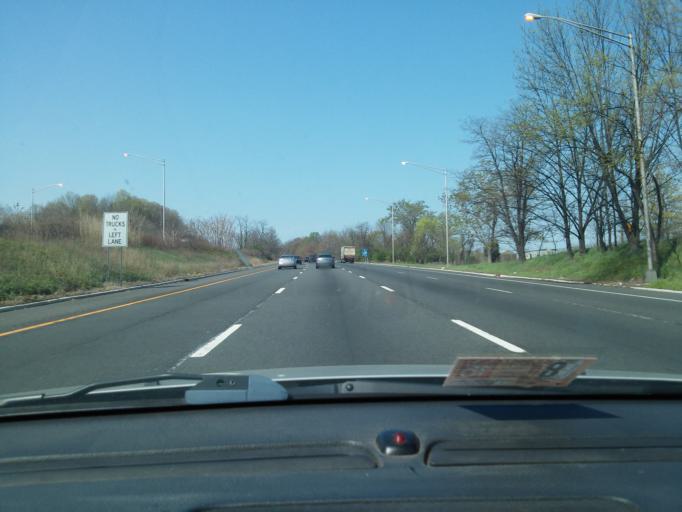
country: US
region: New Jersey
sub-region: Union County
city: Springfield
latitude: 40.7098
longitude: -74.3330
